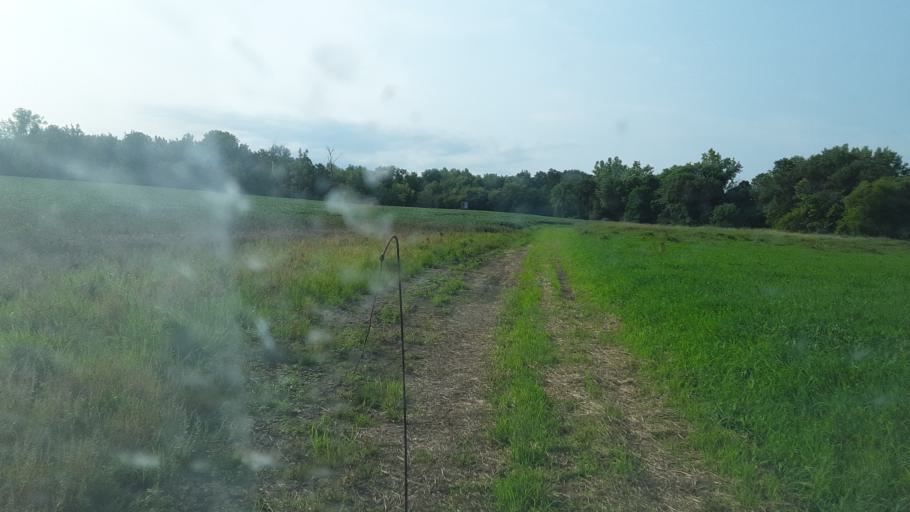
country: US
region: Ohio
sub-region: Crawford County
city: Bucyrus
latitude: 40.6620
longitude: -82.9553
